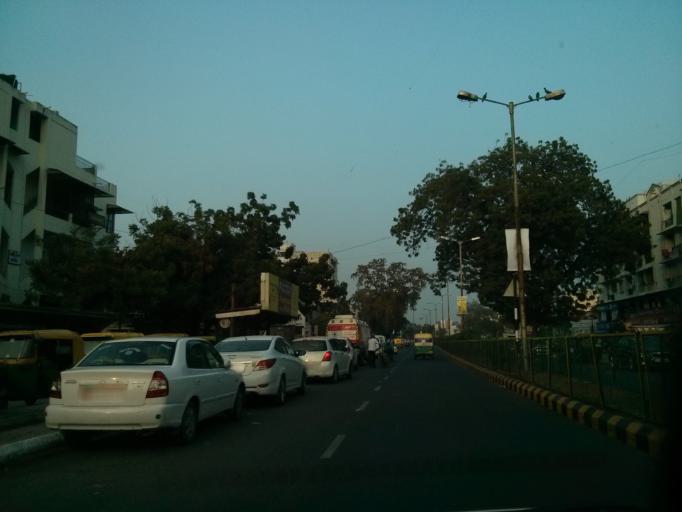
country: IN
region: Gujarat
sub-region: Ahmadabad
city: Ahmedabad
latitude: 23.0552
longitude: 72.5972
